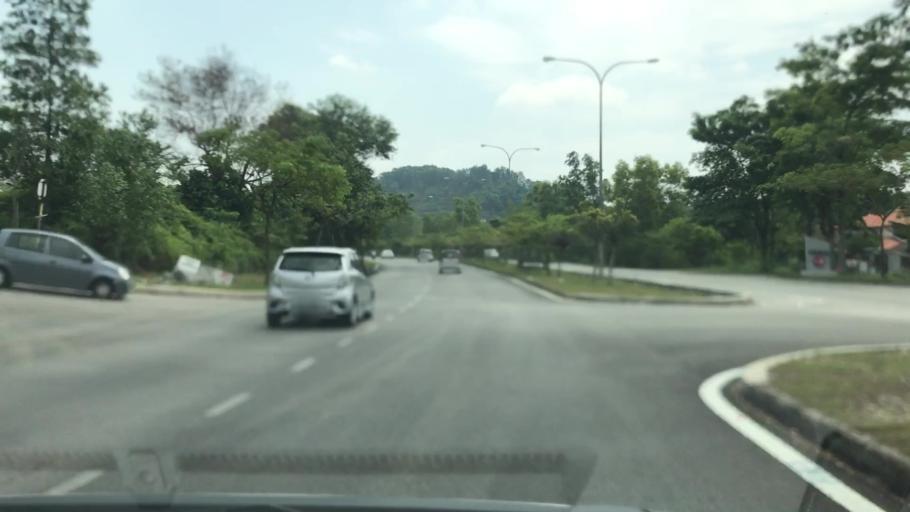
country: MY
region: Putrajaya
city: Putrajaya
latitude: 3.0079
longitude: 101.6705
